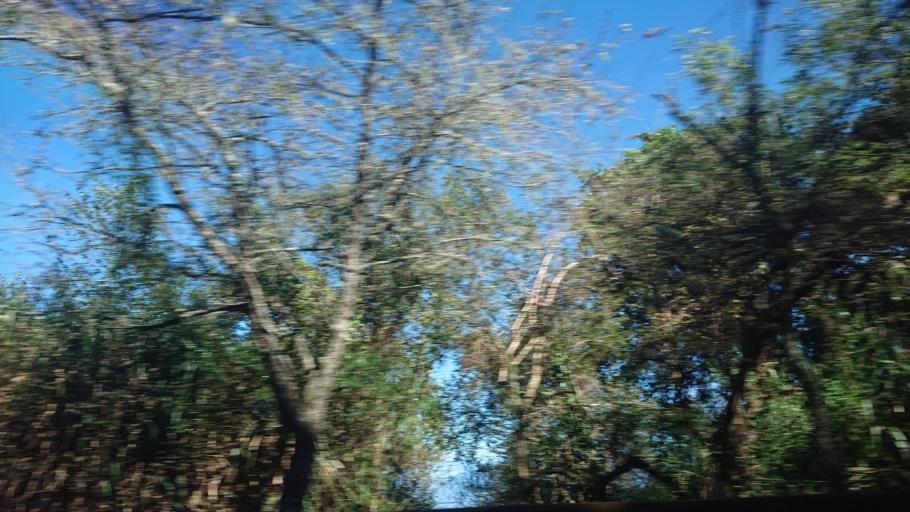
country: TW
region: Taiwan
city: Lugu
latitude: 23.4865
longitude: 120.8534
